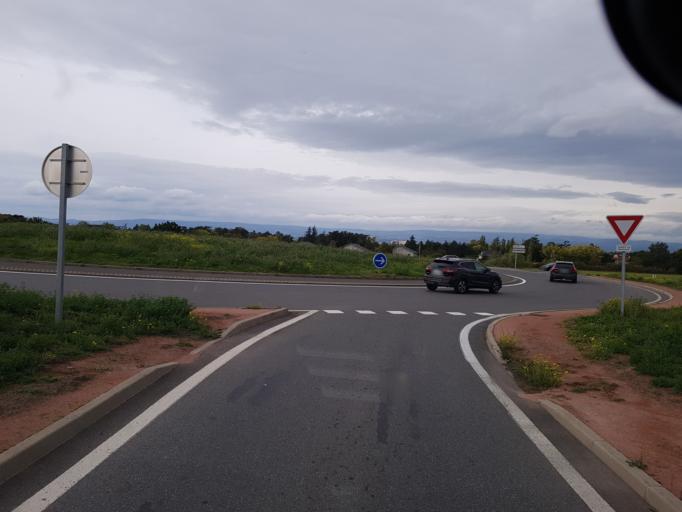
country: FR
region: Rhone-Alpes
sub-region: Departement de la Loire
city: La Fouillouse
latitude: 45.5264
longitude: 4.2981
